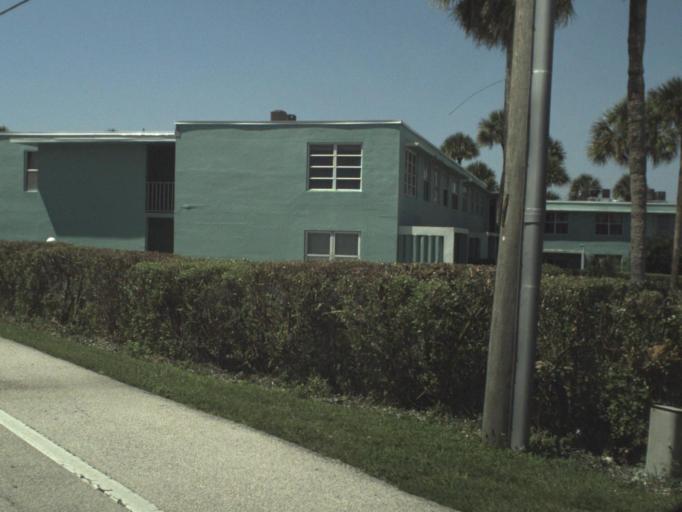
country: US
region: Florida
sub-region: Brevard County
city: South Patrick Shores
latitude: 28.2042
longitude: -80.5967
